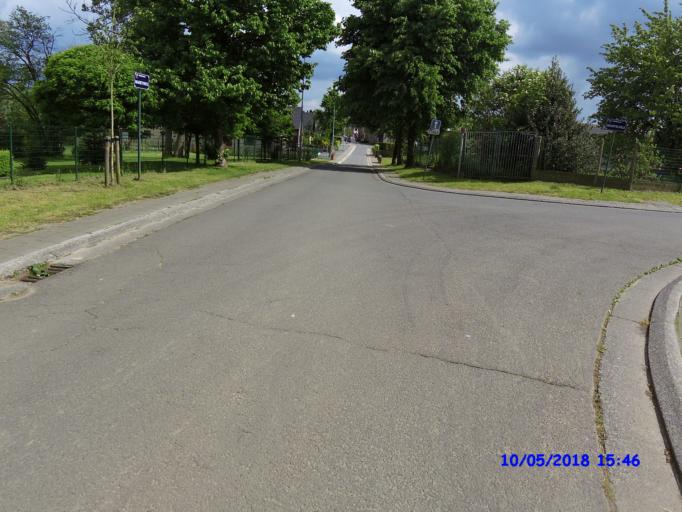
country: BE
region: Flanders
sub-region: Provincie Oost-Vlaanderen
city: Aalst
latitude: 50.9033
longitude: 4.0432
